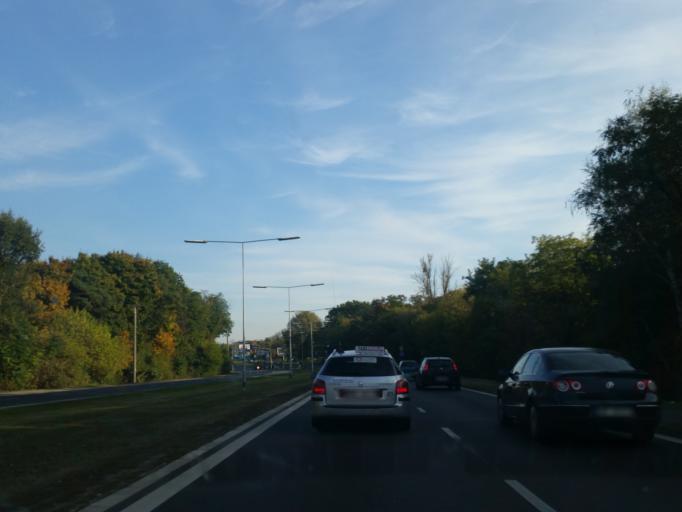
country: PL
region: Masovian Voivodeship
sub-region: Warszawa
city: Bielany
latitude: 52.3105
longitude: 20.9253
